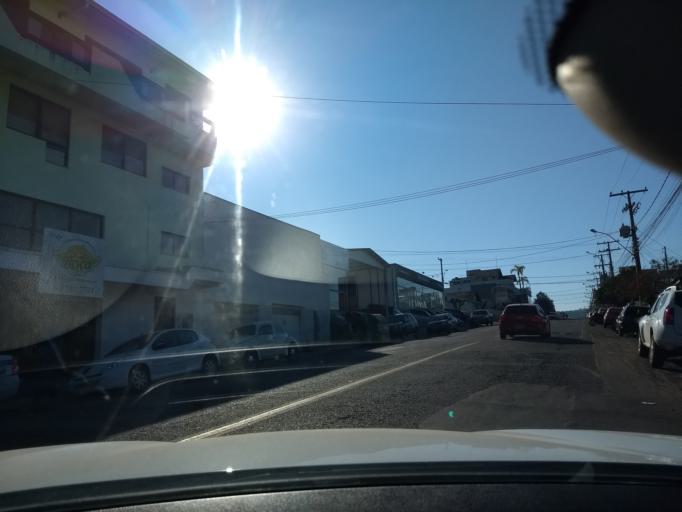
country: BR
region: Rio Grande do Sul
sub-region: Santa Cruz Do Sul
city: Santa Cruz do Sul
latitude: -29.7161
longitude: -52.4414
